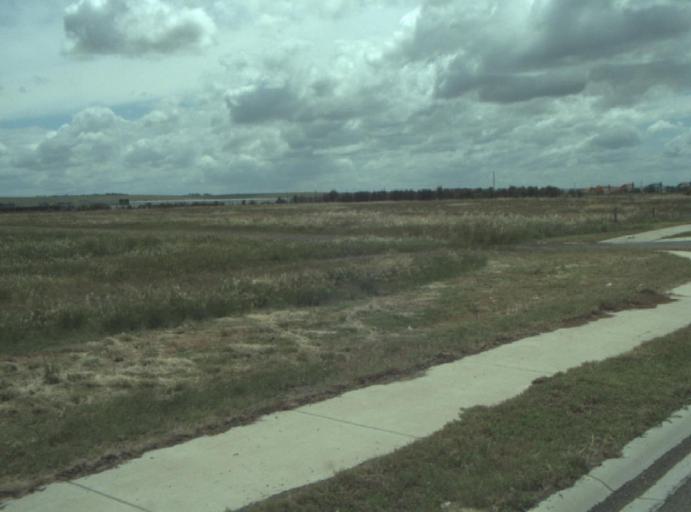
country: AU
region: Victoria
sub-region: Greater Geelong
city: Lara
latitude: -38.0618
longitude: 144.3779
